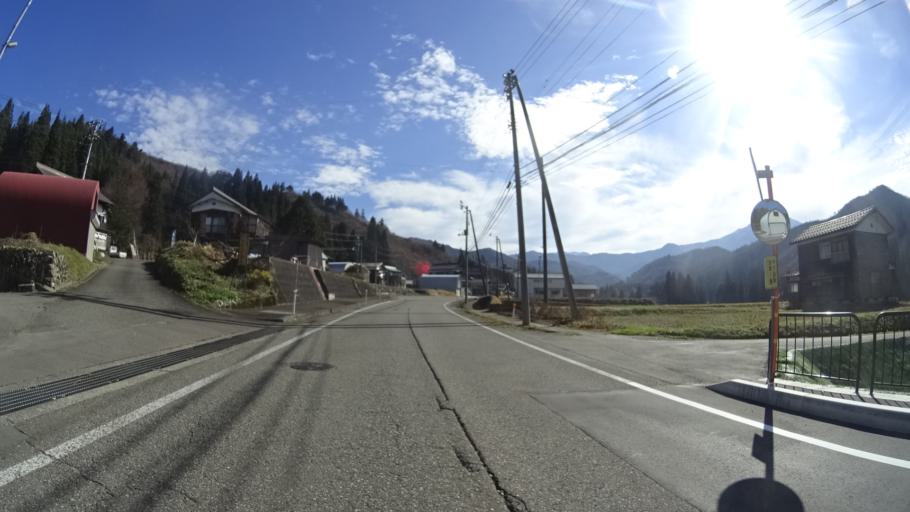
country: JP
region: Niigata
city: Muikamachi
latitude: 37.2036
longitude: 139.0735
